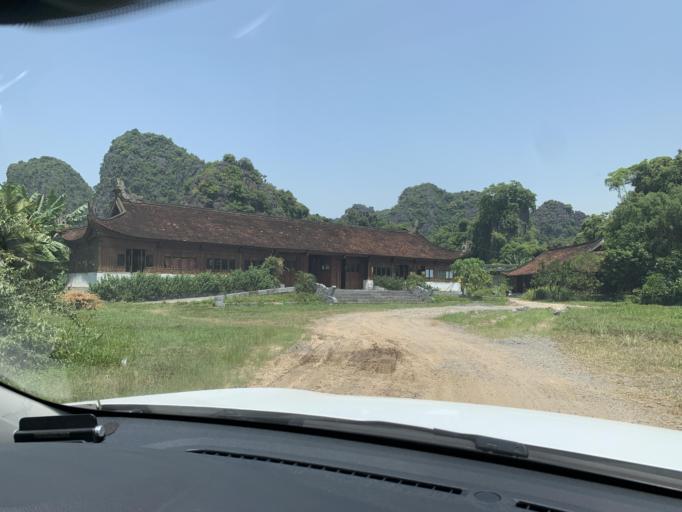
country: VN
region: Ninh Binh
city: Thanh Pho Ninh Binh
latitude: 20.2235
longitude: 105.9285
